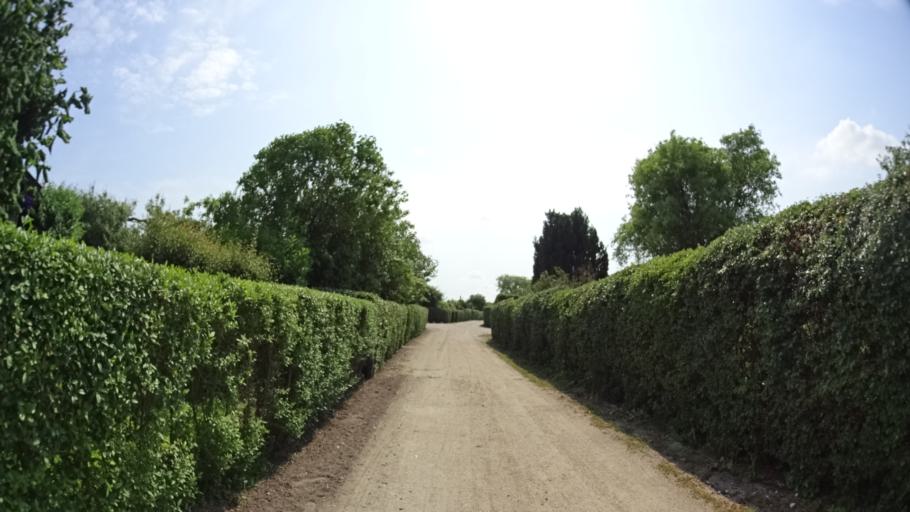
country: DK
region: Central Jutland
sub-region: Arhus Kommune
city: Arhus
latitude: 56.1459
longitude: 10.1660
